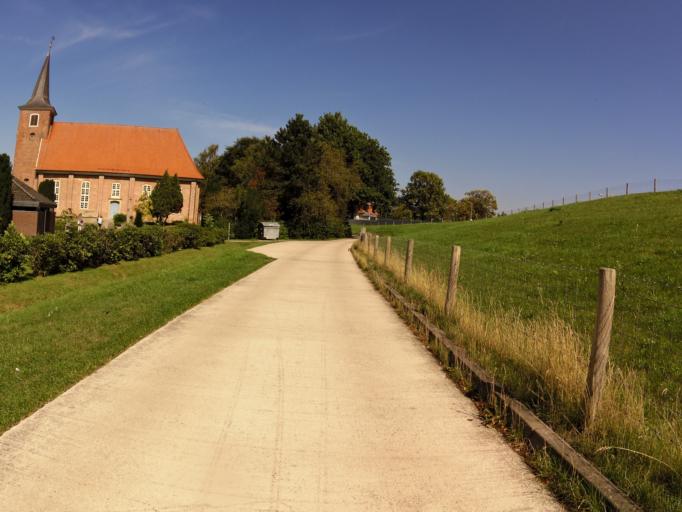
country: DE
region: Lower Saxony
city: Brake (Unterweser)
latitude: 53.3049
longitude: 8.4866
